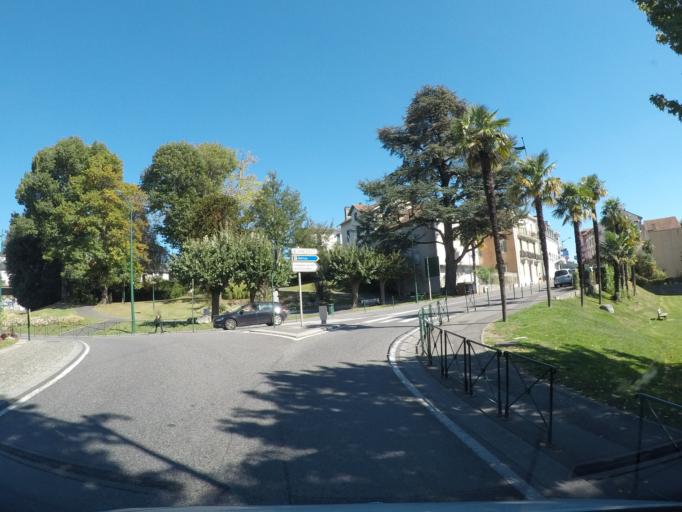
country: FR
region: Midi-Pyrenees
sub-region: Departement des Hautes-Pyrenees
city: Lourdes
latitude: 43.0993
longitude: -0.0451
